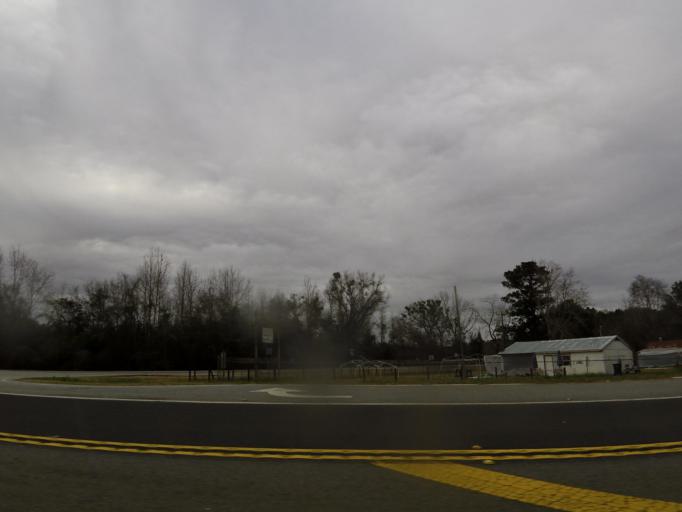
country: US
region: Georgia
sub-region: Randolph County
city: Shellman
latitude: 31.7811
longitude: -84.6023
